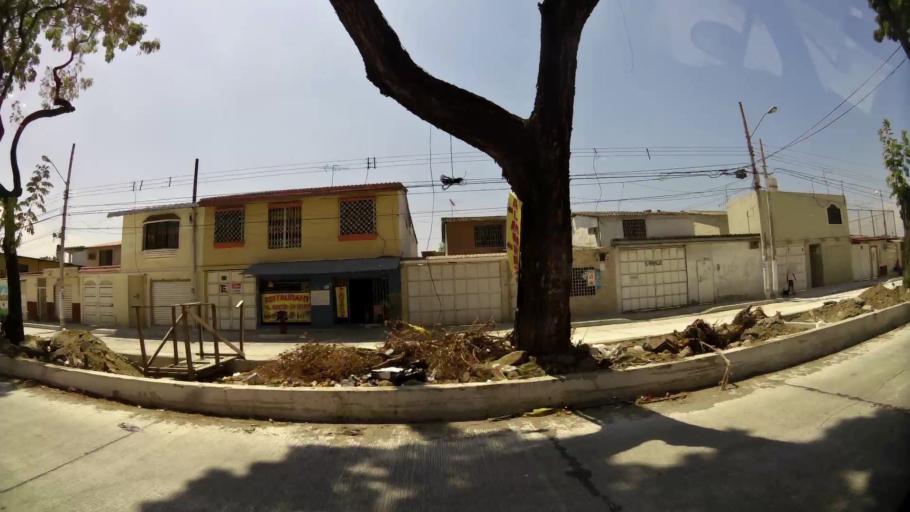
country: EC
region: Guayas
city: Eloy Alfaro
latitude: -2.1135
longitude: -79.9016
